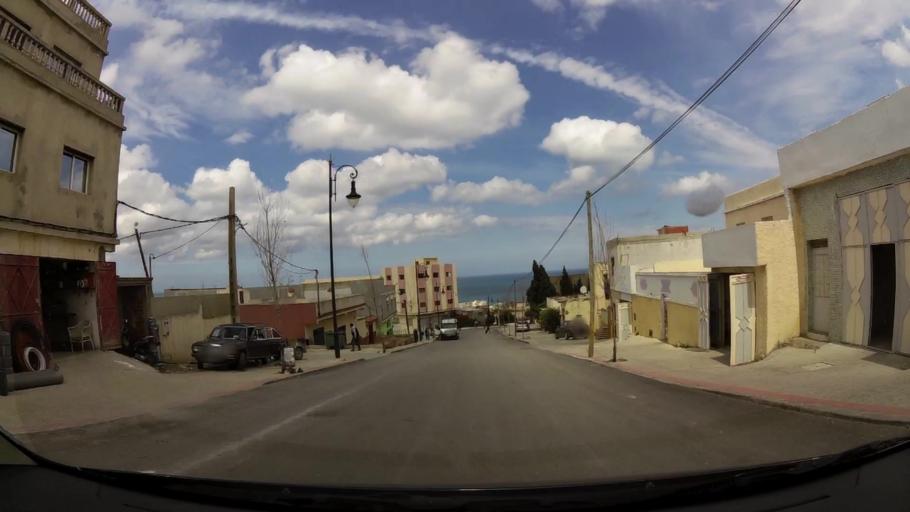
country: MA
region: Tanger-Tetouan
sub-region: Tanger-Assilah
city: Tangier
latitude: 35.7776
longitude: -5.7537
